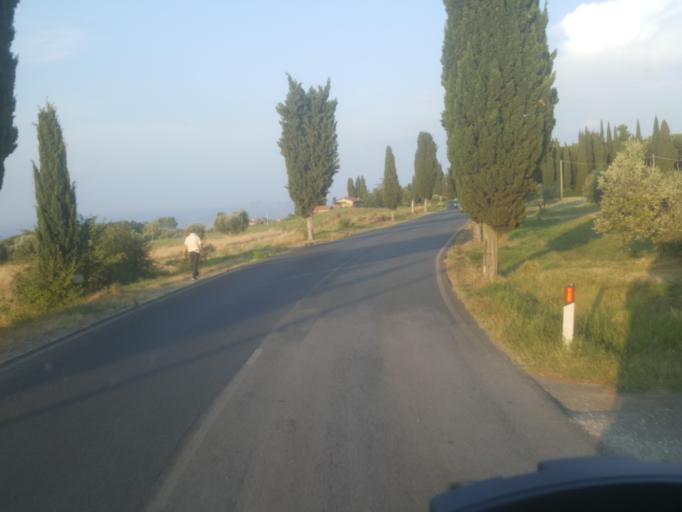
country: IT
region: Tuscany
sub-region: Province of Florence
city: Gambassi Terme
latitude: 43.5323
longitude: 10.9388
